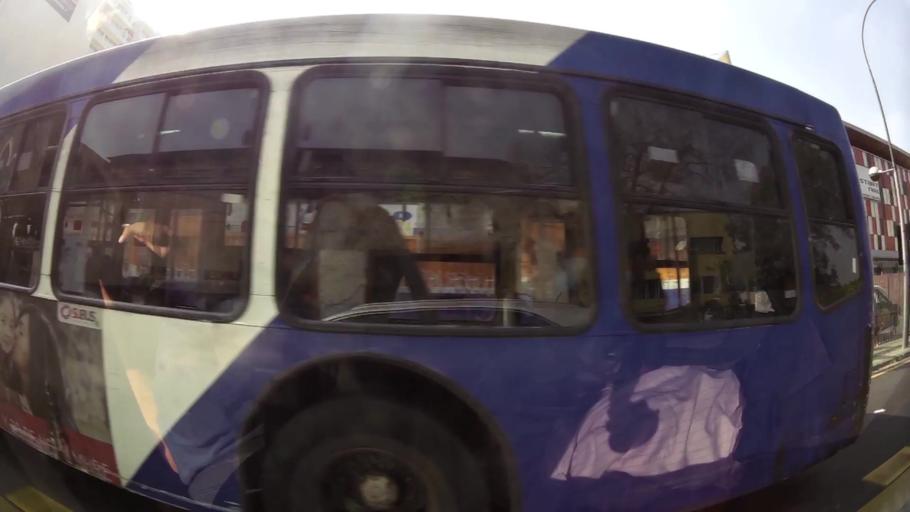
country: CL
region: Santiago Metropolitan
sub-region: Provincia de Santiago
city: Santiago
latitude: -33.4526
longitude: -70.6440
